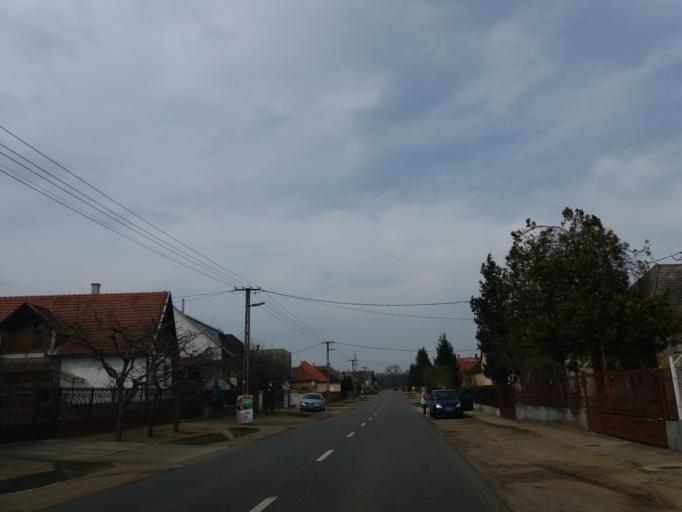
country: HU
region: Szabolcs-Szatmar-Bereg
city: Anarcs
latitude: 48.1816
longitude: 22.1012
